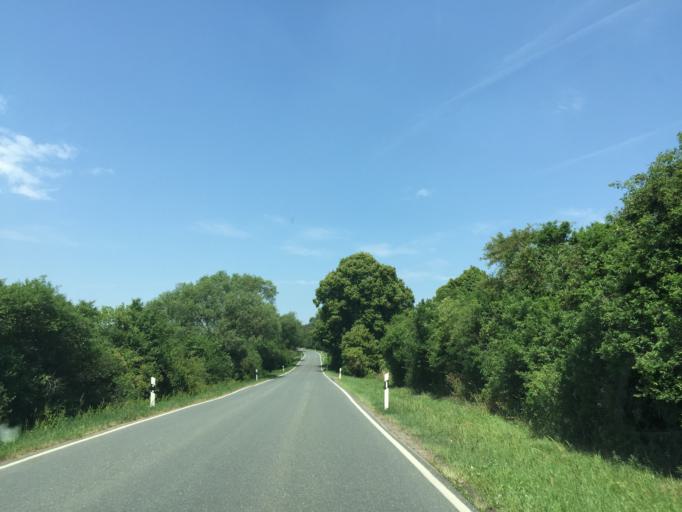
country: DE
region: Thuringia
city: Rittersdorf
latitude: 50.7755
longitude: 11.2192
